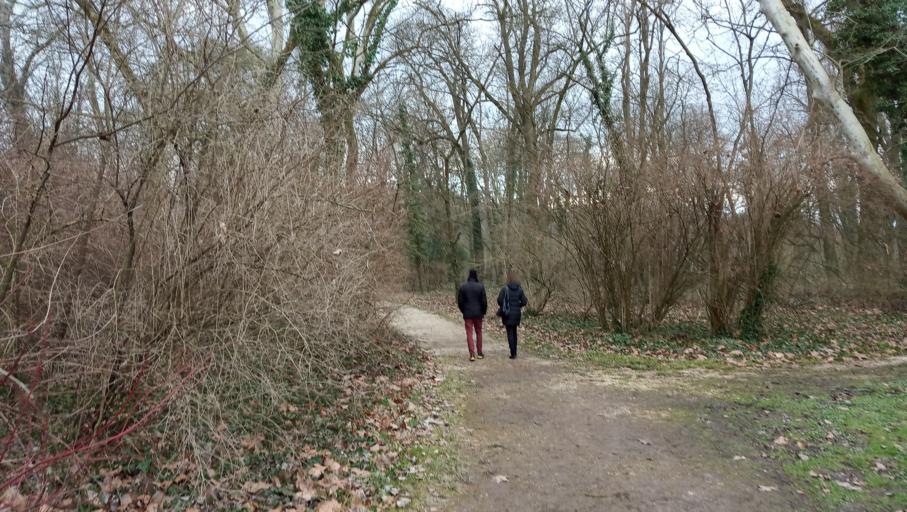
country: HU
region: Fejer
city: Bicske
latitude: 47.4254
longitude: 18.5952
